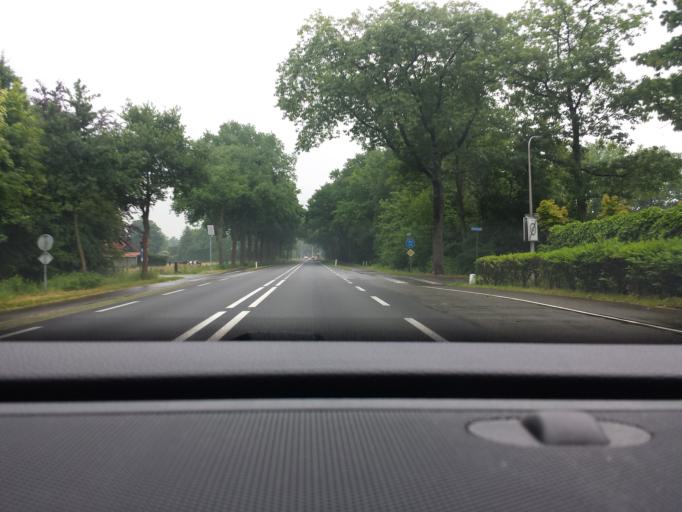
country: NL
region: Overijssel
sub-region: Gemeente Enschede
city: Enschede
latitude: 52.1982
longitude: 6.8303
